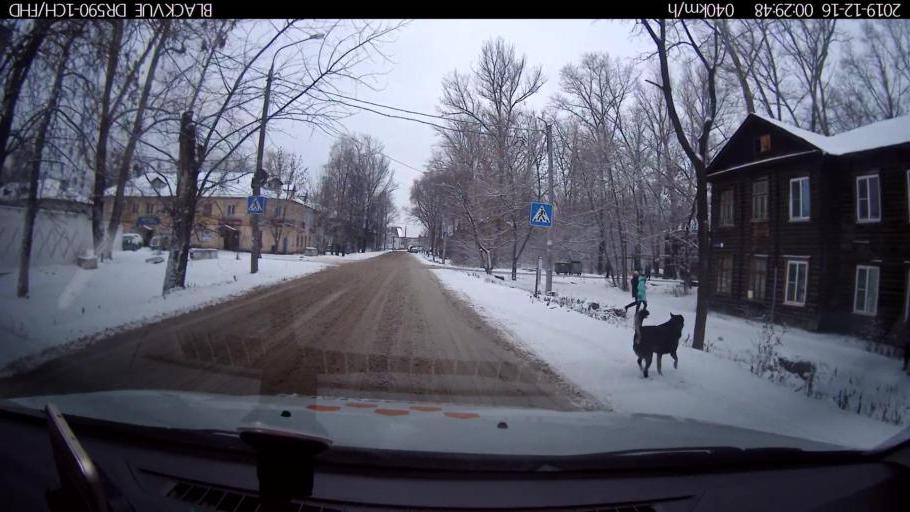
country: RU
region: Nizjnij Novgorod
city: Nizhniy Novgorod
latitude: 56.3100
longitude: 43.8906
